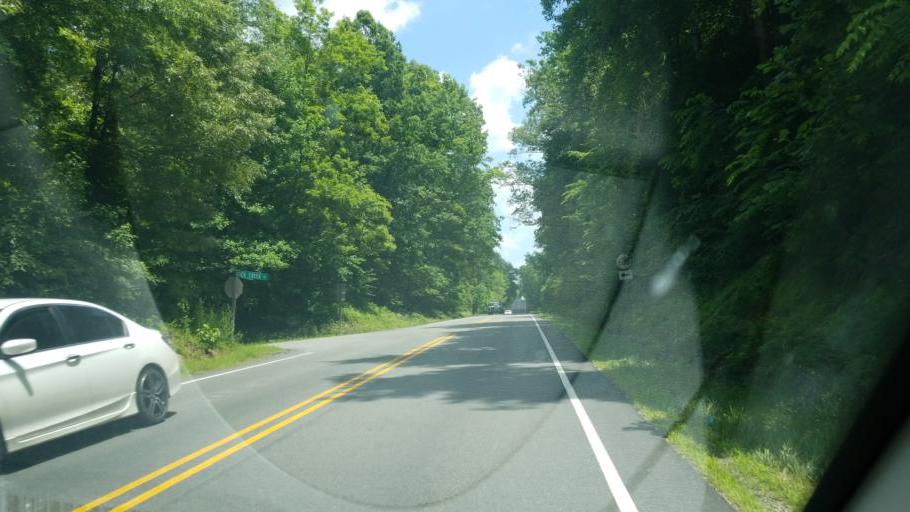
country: US
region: Virginia
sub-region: Cumberland County
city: Cumberland
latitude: 37.4836
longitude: -78.3191
